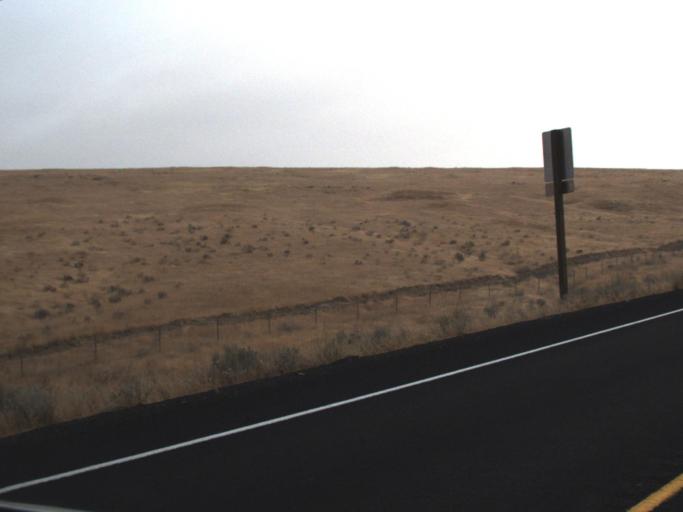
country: US
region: Washington
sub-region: Yakima County
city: Toppenish
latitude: 46.2774
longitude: -120.3860
